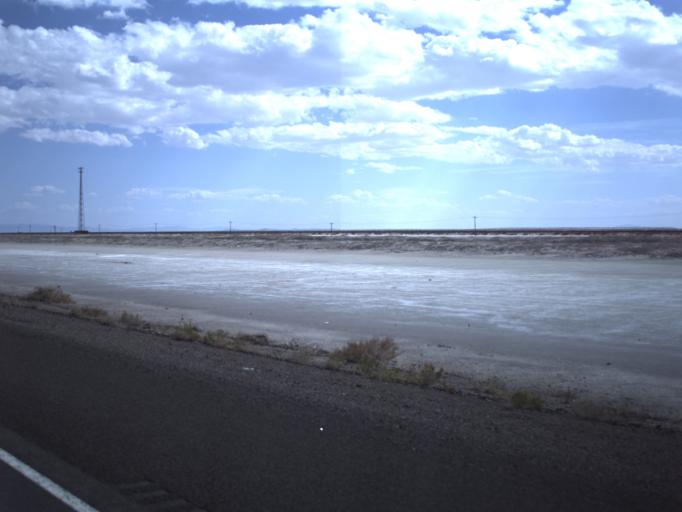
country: US
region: Utah
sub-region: Tooele County
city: Wendover
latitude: 40.7374
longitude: -113.8003
